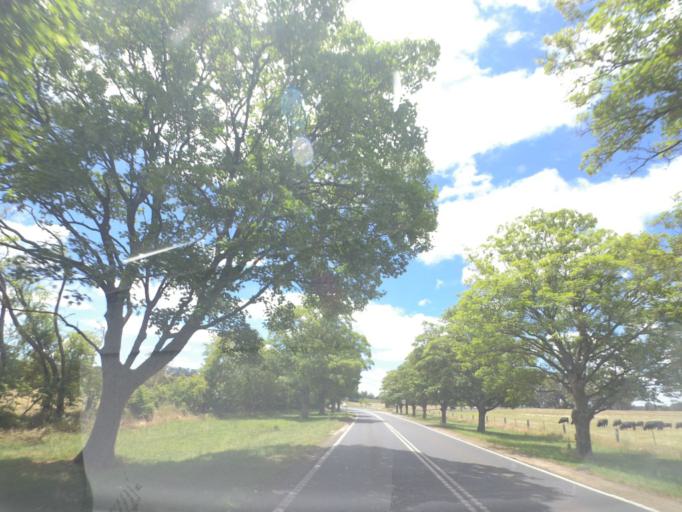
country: AU
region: Victoria
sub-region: Mount Alexander
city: Castlemaine
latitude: -37.3361
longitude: 144.1637
